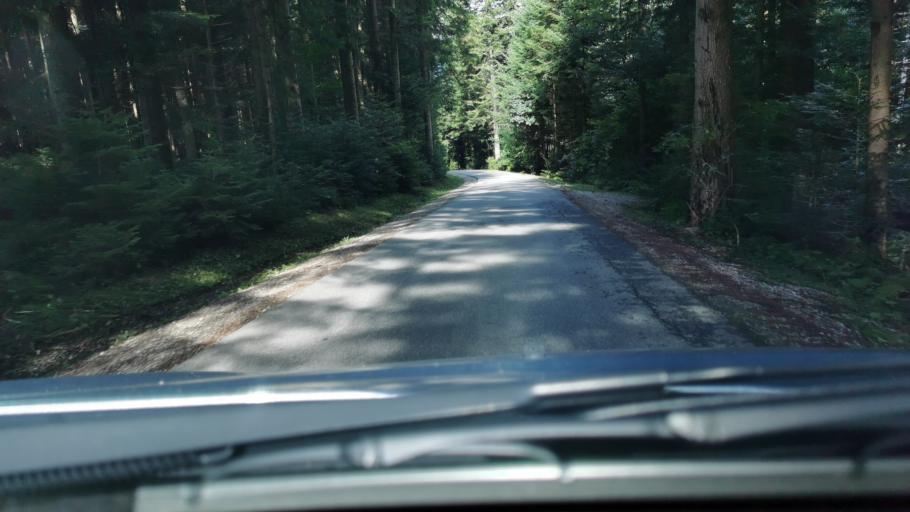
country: AT
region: Styria
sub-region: Politischer Bezirk Weiz
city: Gschaid bei Birkfeld
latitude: 47.3295
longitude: 15.7094
